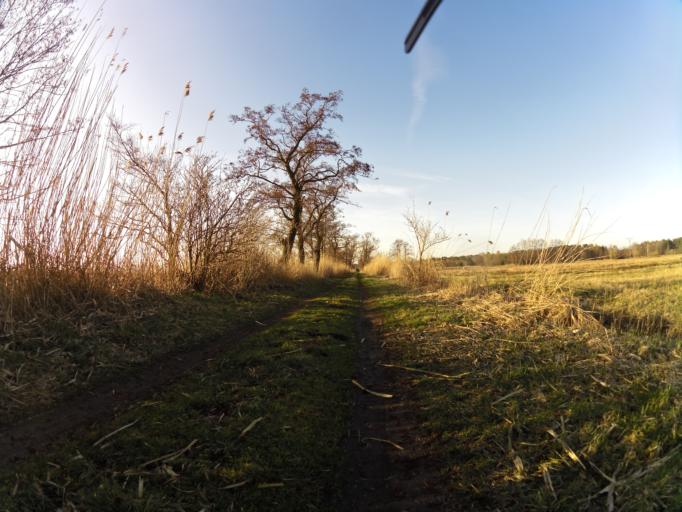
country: PL
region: West Pomeranian Voivodeship
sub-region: Powiat policki
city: Nowe Warpno
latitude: 53.7301
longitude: 14.3044
